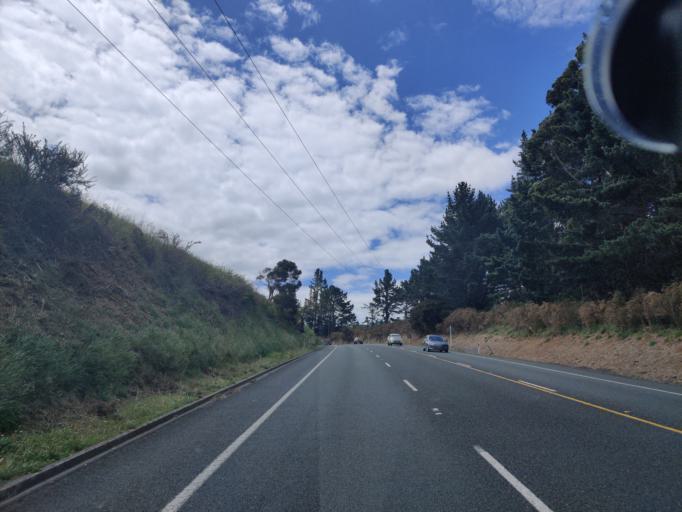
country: NZ
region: Northland
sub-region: Far North District
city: Kerikeri
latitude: -35.2836
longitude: 173.9562
